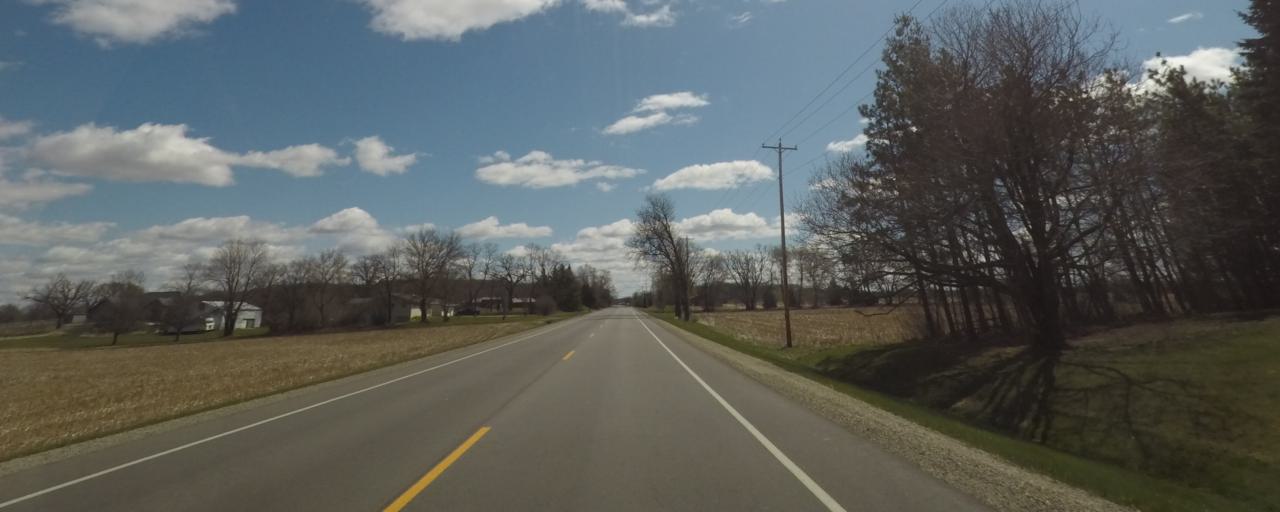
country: US
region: Wisconsin
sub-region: Jefferson County
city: Lake Mills
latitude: 43.0885
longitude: -88.9703
